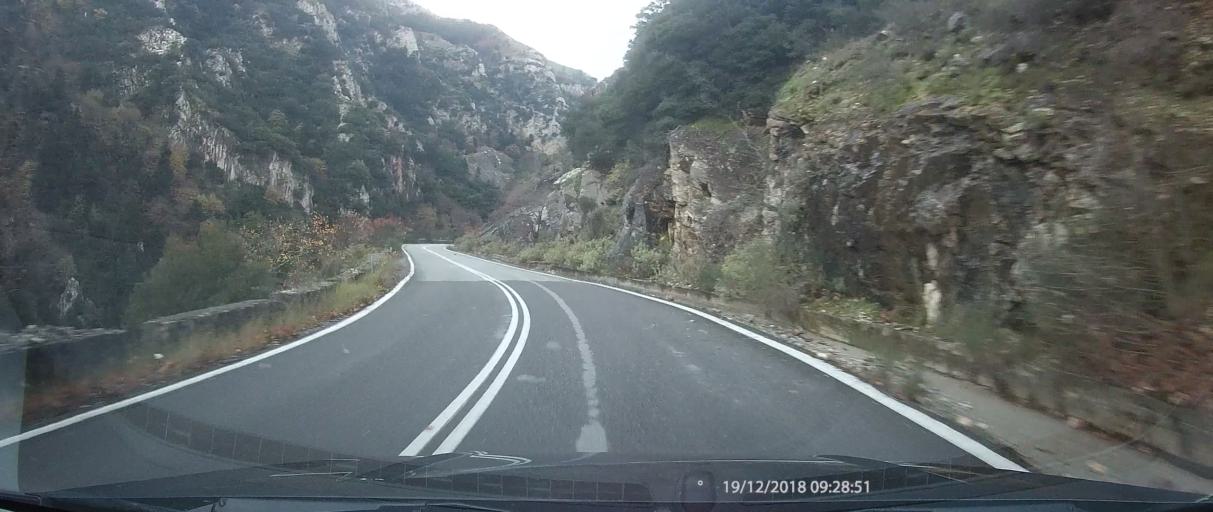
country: GR
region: Peloponnese
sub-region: Nomos Lakonias
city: Magoula
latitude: 37.0887
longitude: 22.3212
